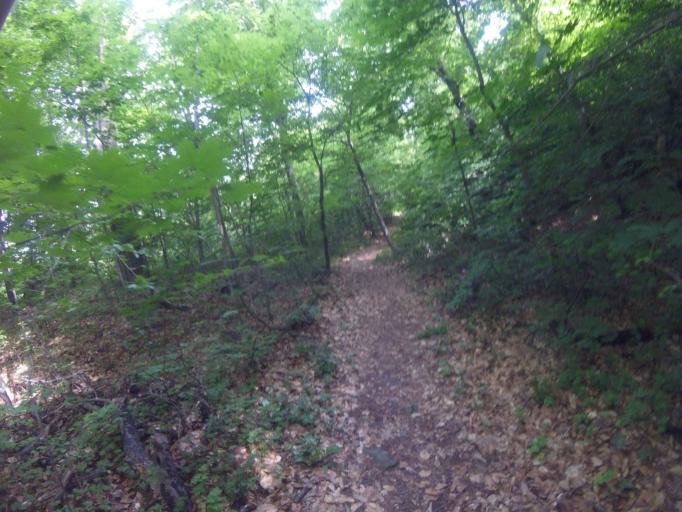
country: HU
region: Zala
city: Turje
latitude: 46.9088
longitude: 17.1731
